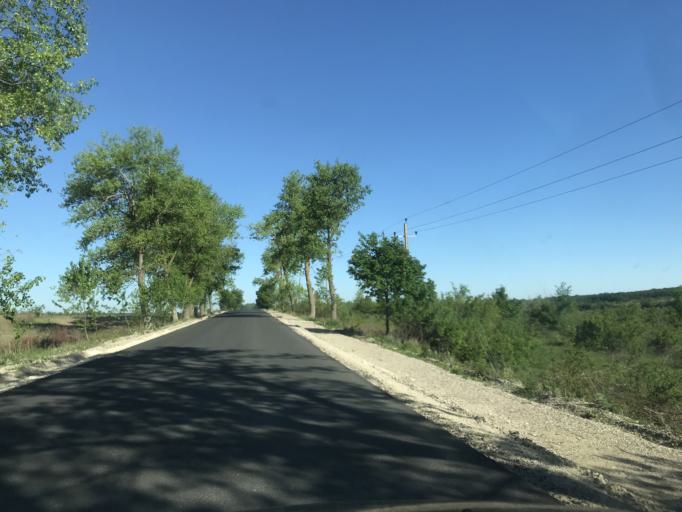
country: MD
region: Chisinau
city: Cricova
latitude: 47.2515
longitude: 28.8127
